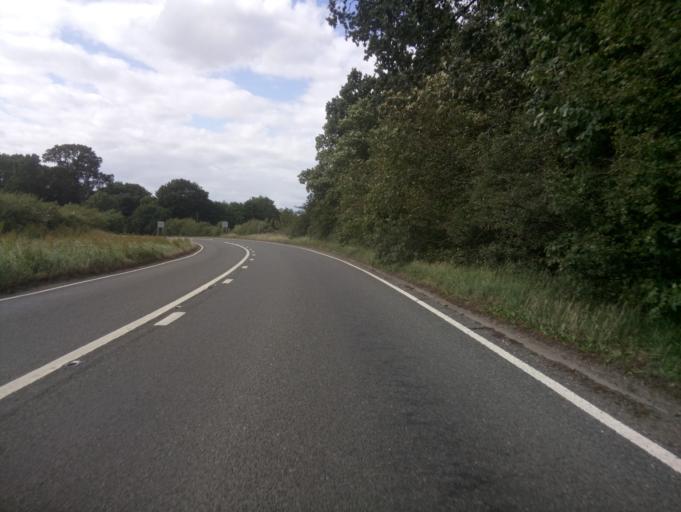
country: GB
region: England
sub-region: Leicestershire
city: Measham
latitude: 52.6739
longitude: -1.5417
